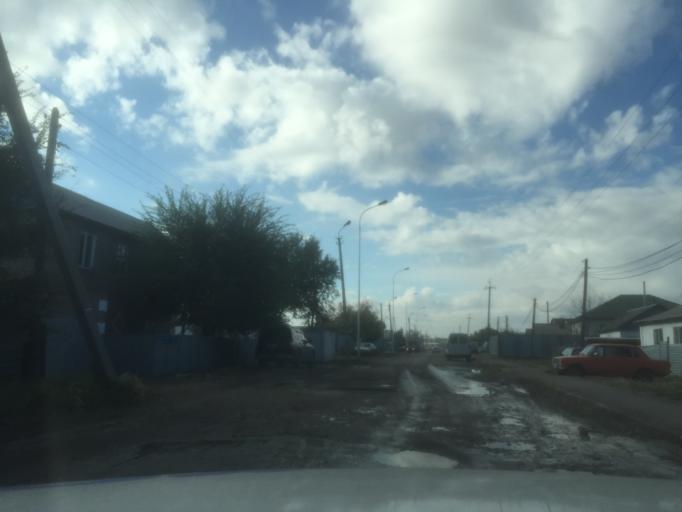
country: KZ
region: Astana Qalasy
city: Astana
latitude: 51.1875
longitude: 71.3934
